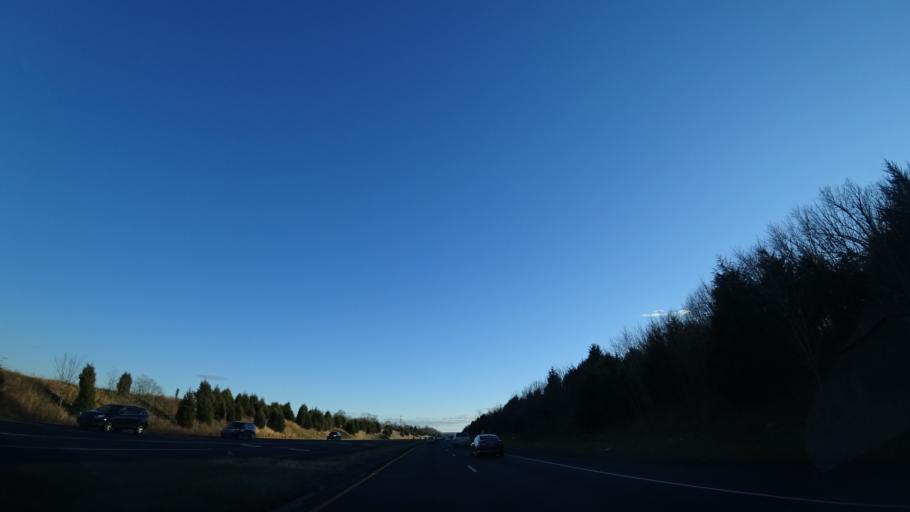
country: US
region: Virginia
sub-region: Prince William County
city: Bull Run
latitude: 38.7663
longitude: -77.5347
